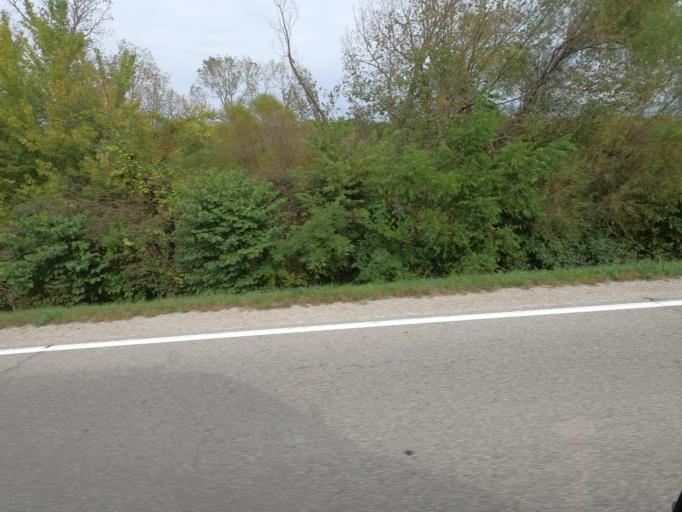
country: US
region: Iowa
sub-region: Jefferson County
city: Fairfield
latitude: 40.8781
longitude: -92.1571
